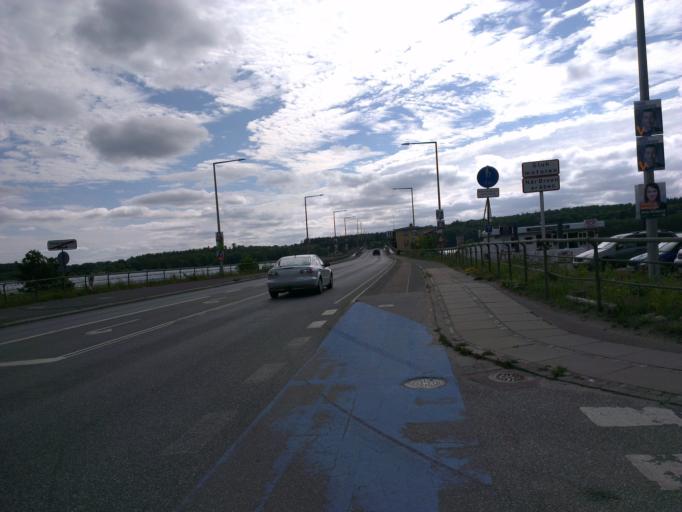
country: DK
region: Capital Region
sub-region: Frederikssund Kommune
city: Frederikssund
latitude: 55.8443
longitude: 12.0439
